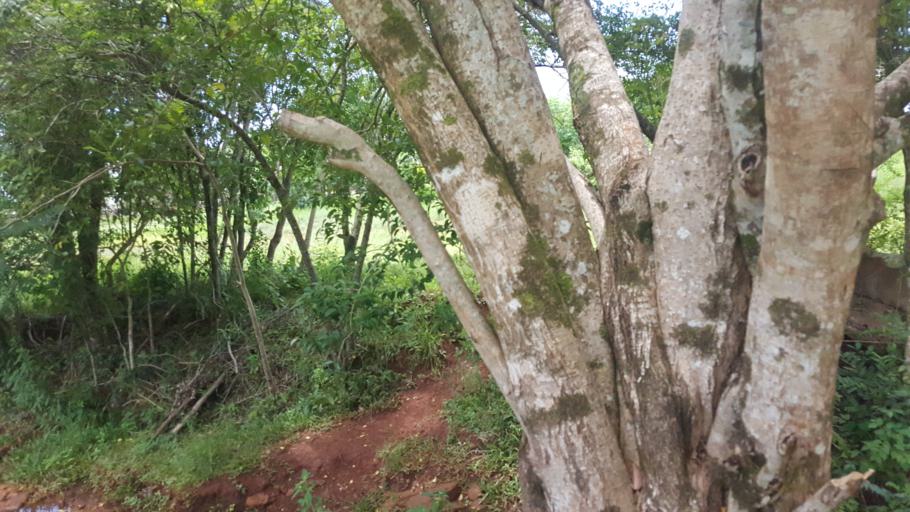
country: AR
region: Misiones
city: Capiovi
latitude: -26.9307
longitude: -55.0534
